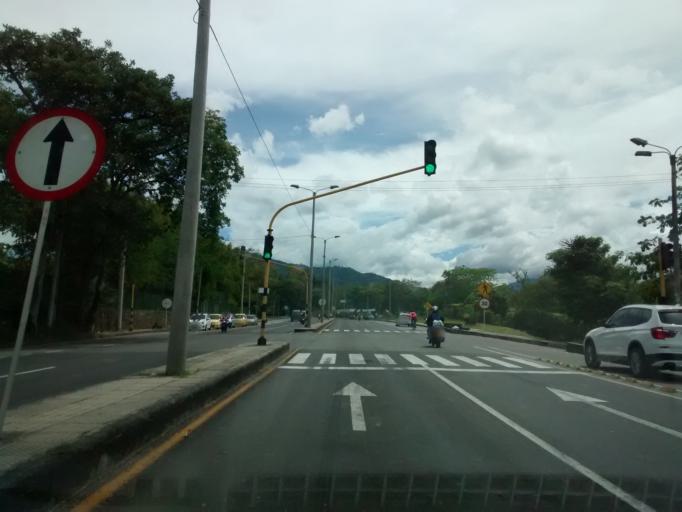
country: CO
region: Tolima
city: Ibague
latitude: 4.4044
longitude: -75.1600
